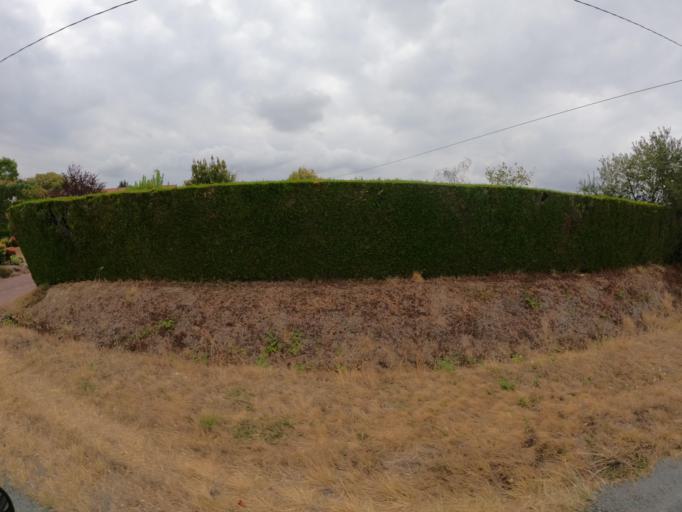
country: FR
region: Pays de la Loire
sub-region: Departement de Maine-et-Loire
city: Le Longeron
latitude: 47.0284
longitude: -1.0478
